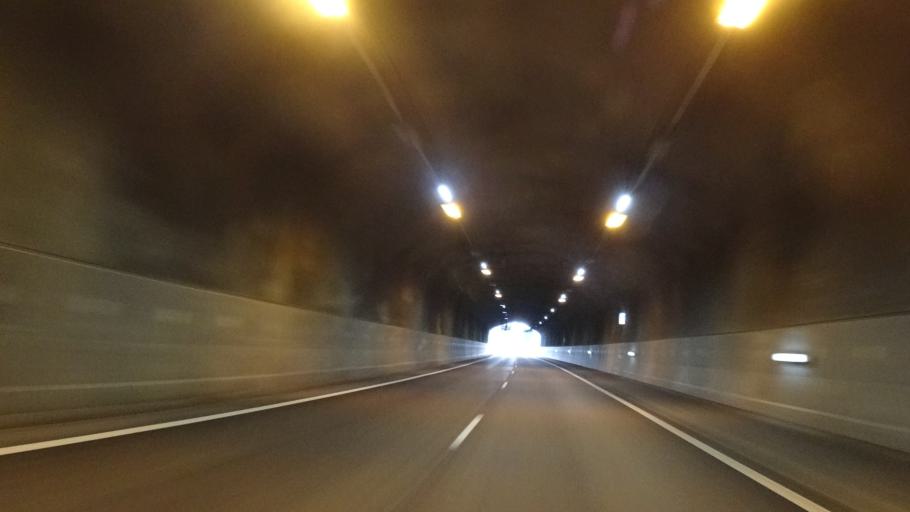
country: FI
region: Kymenlaakso
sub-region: Kotka-Hamina
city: Virojoki
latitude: 60.6130
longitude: 27.7927
